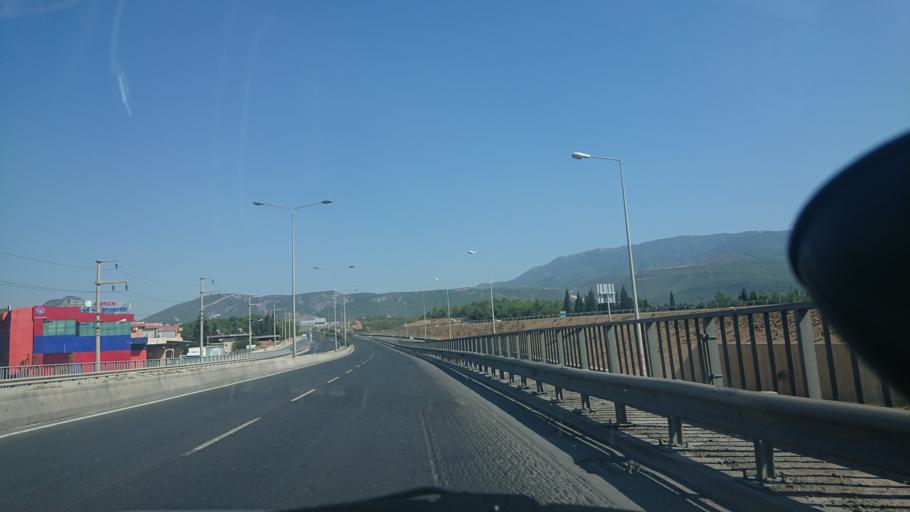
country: TR
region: Izmir
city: Bornova
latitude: 38.4519
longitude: 27.2674
